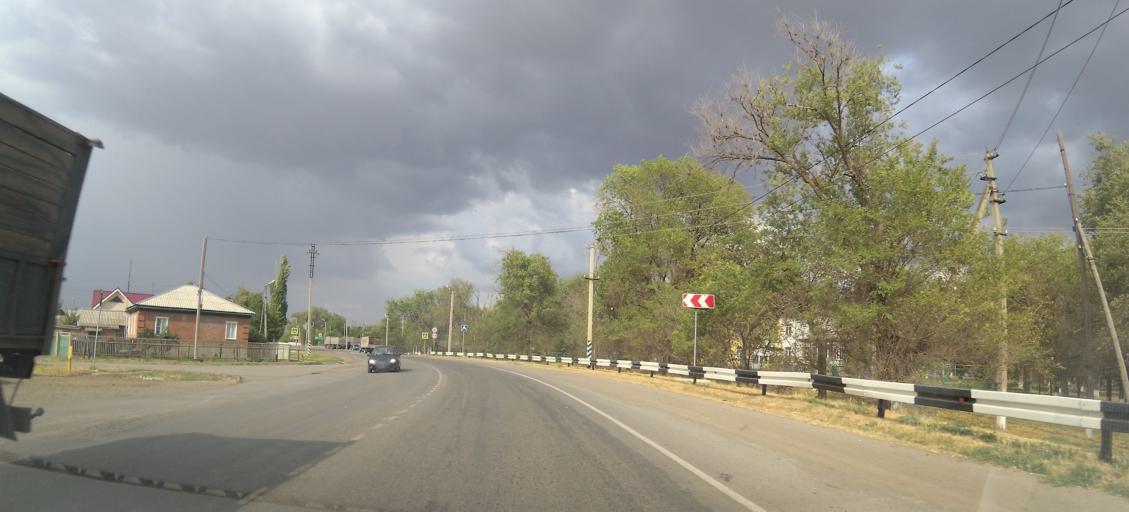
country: RU
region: Rostov
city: Zimovniki
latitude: 47.1466
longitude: 42.4580
